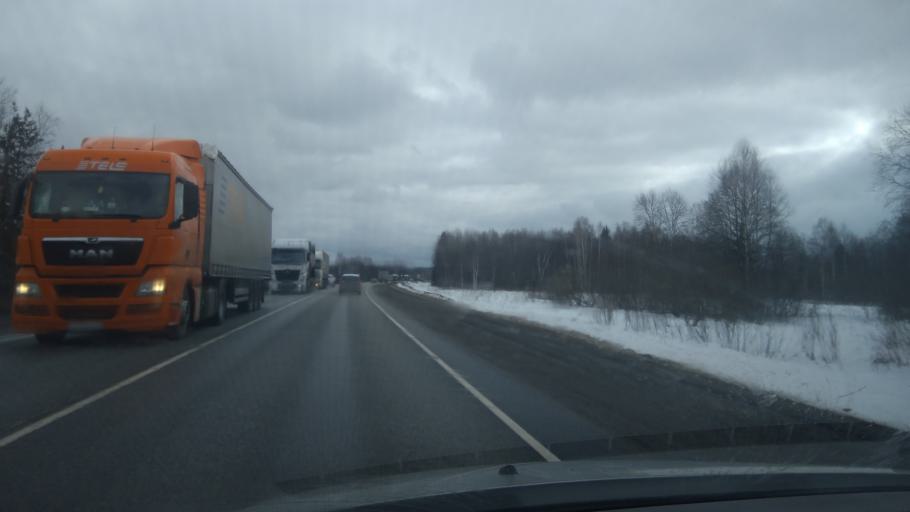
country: RU
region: Sverdlovsk
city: Ufimskiy
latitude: 56.7702
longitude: 58.1229
